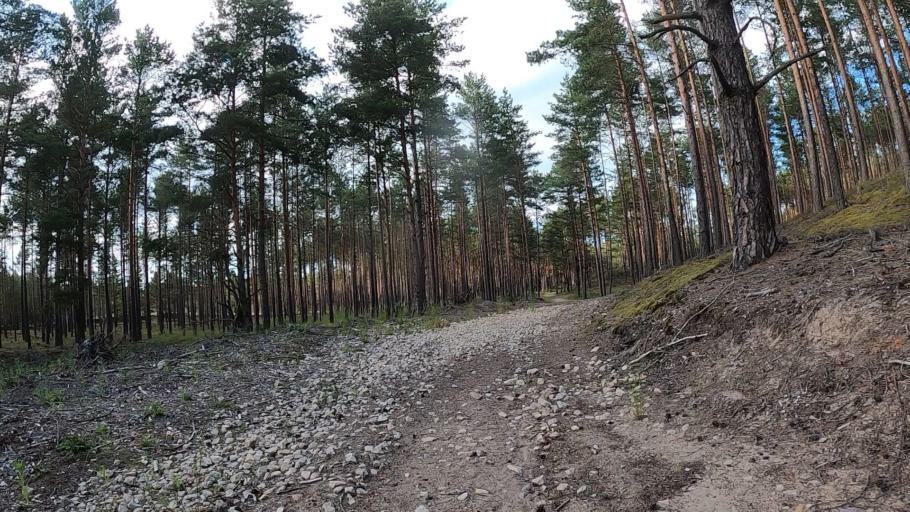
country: LV
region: Riga
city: Jaunciems
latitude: 57.0574
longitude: 24.1252
